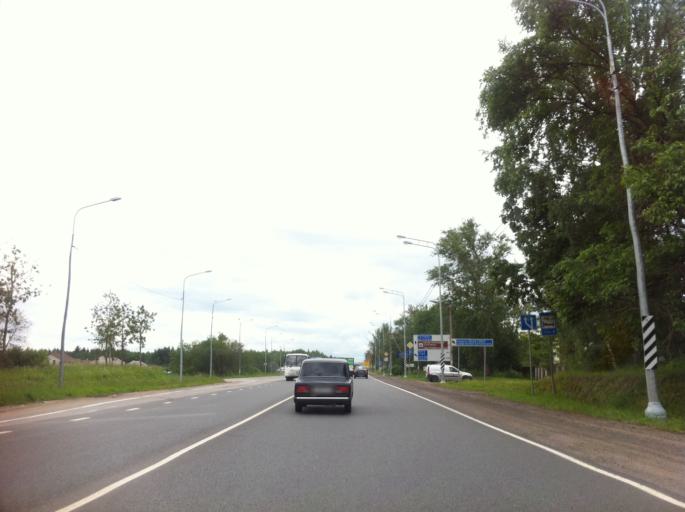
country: RU
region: Leningrad
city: Maloye Verevo
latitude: 59.6013
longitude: 30.1601
